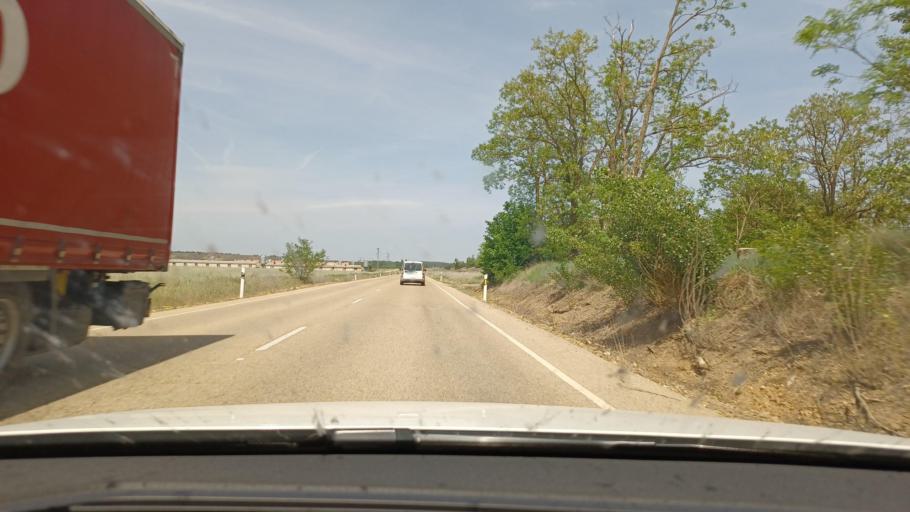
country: ES
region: Castille and Leon
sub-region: Provincia de Soria
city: Barca
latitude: 41.4687
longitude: -2.6058
